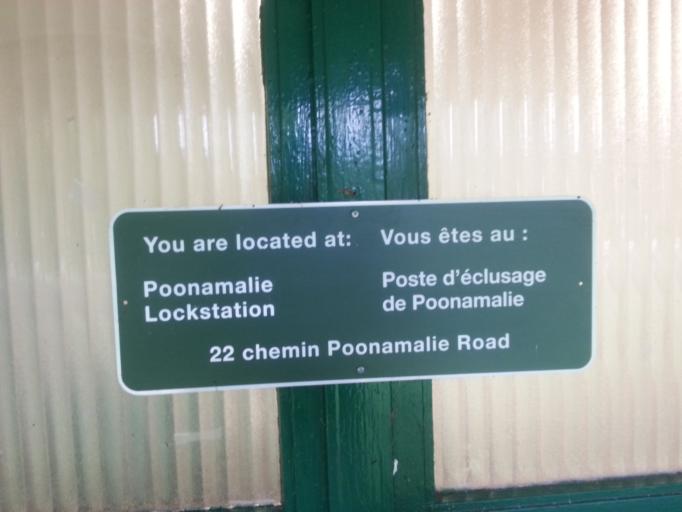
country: CA
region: Ontario
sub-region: Lanark County
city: Smiths Falls
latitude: 44.8929
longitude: -76.0555
